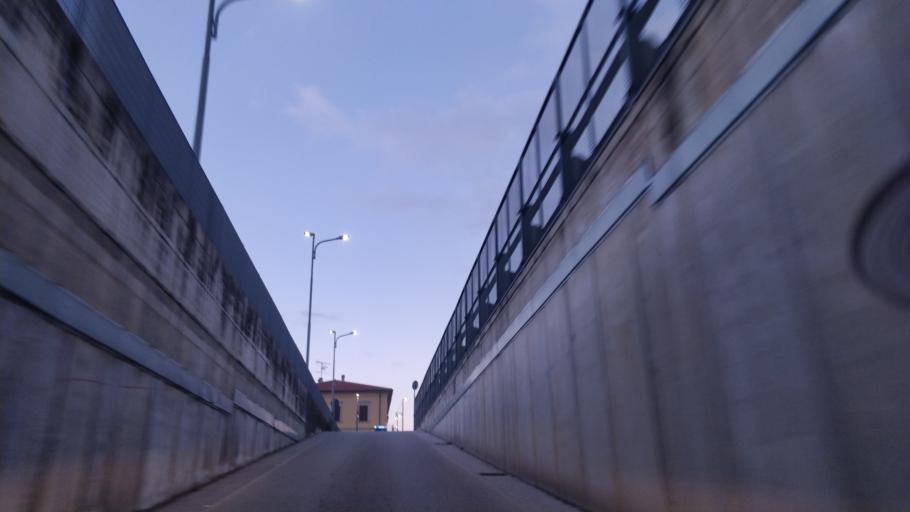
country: IT
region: Tuscany
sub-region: Provincia di Livorno
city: Rosignano Solvay-Castiglioncello
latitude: 43.3868
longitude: 10.4388
